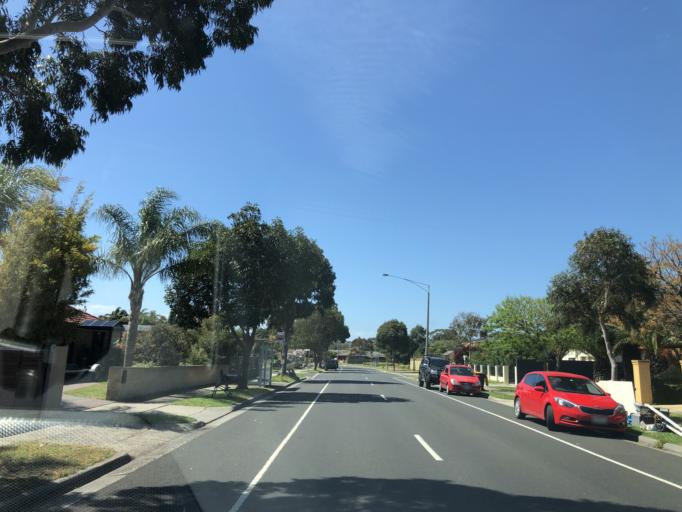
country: AU
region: Victoria
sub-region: Kingston
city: Patterson Lakes
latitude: -38.0789
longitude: 145.1424
